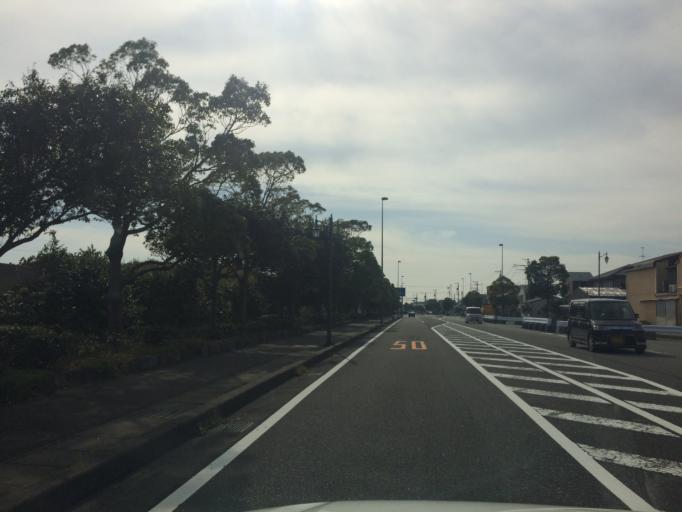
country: JP
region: Shizuoka
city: Yaizu
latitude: 34.8647
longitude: 138.3254
